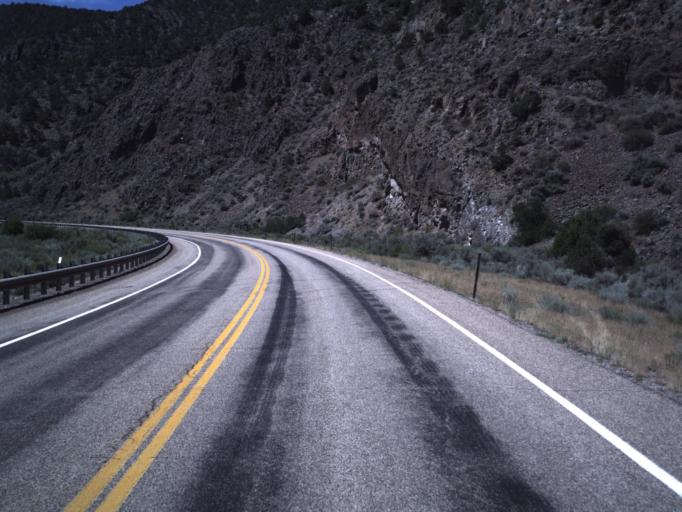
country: US
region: Utah
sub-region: Piute County
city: Junction
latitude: 38.1197
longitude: -112.3366
